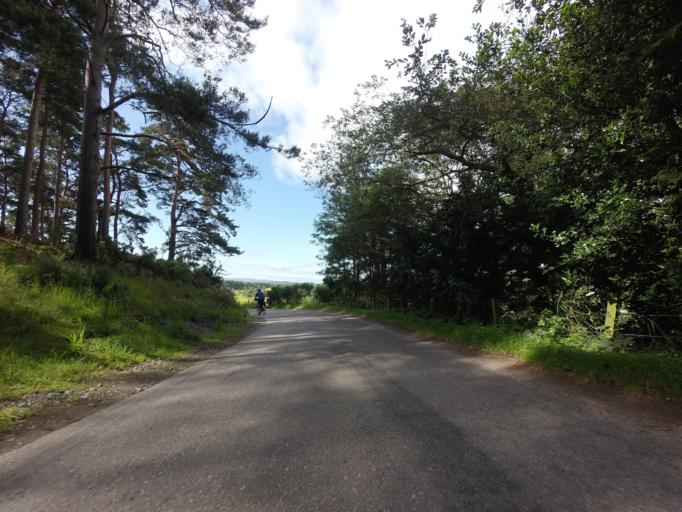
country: GB
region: Scotland
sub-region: Highland
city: Nairn
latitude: 57.5564
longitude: -3.8669
